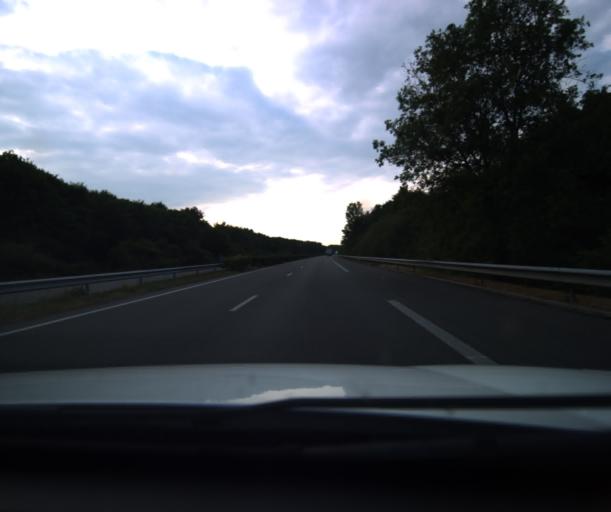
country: FR
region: Midi-Pyrenees
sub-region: Departement du Tarn-et-Garonne
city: Montech
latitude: 43.9894
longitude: 1.2373
